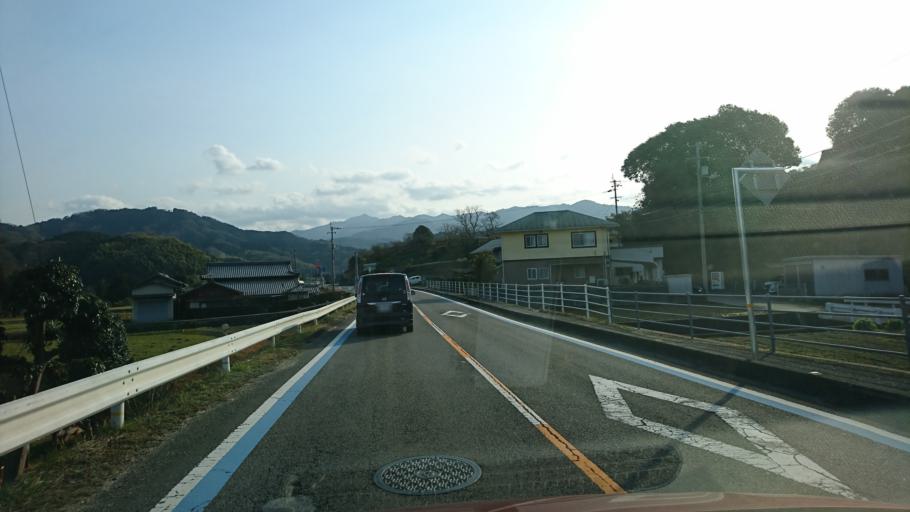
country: JP
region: Ehime
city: Hojo
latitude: 34.0068
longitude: 132.9384
